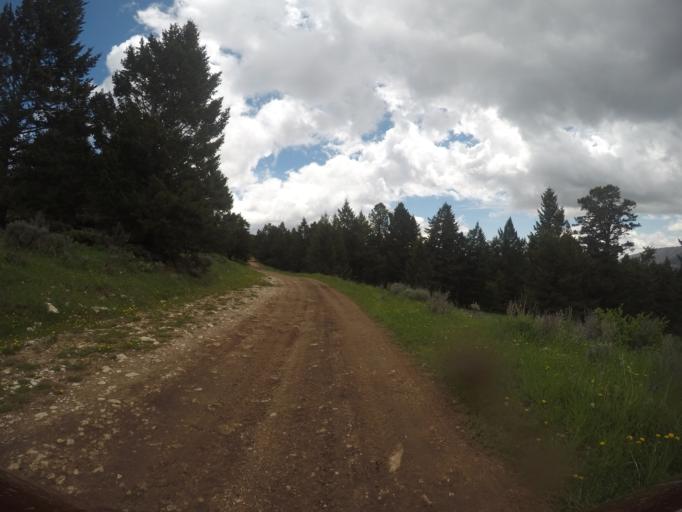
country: US
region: Wyoming
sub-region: Big Horn County
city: Lovell
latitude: 45.1719
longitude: -108.4334
